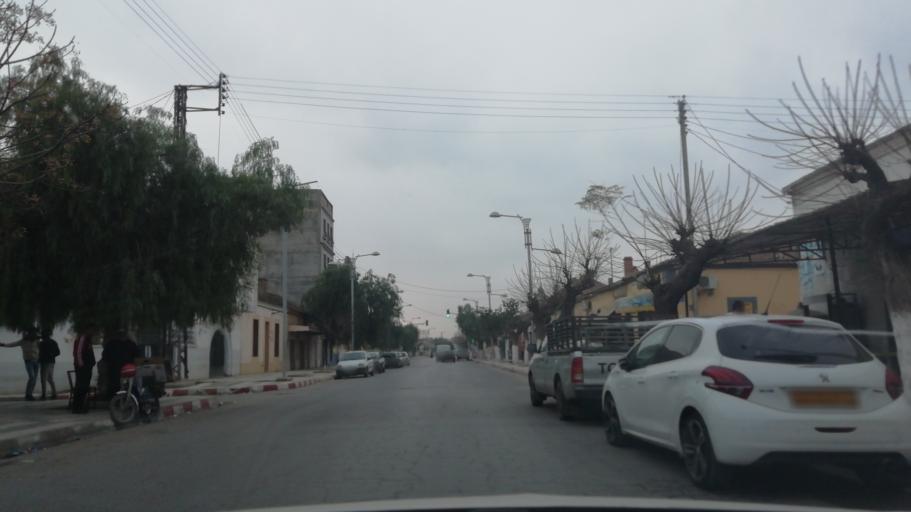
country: DZ
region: Sidi Bel Abbes
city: Sfizef
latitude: 35.2342
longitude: -0.2440
